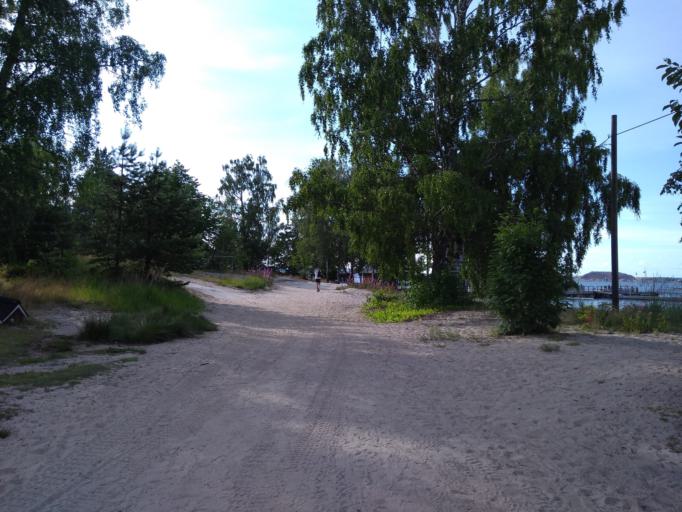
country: FI
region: Uusimaa
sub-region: Helsinki
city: Helsinki
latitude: 60.1396
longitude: 24.9172
